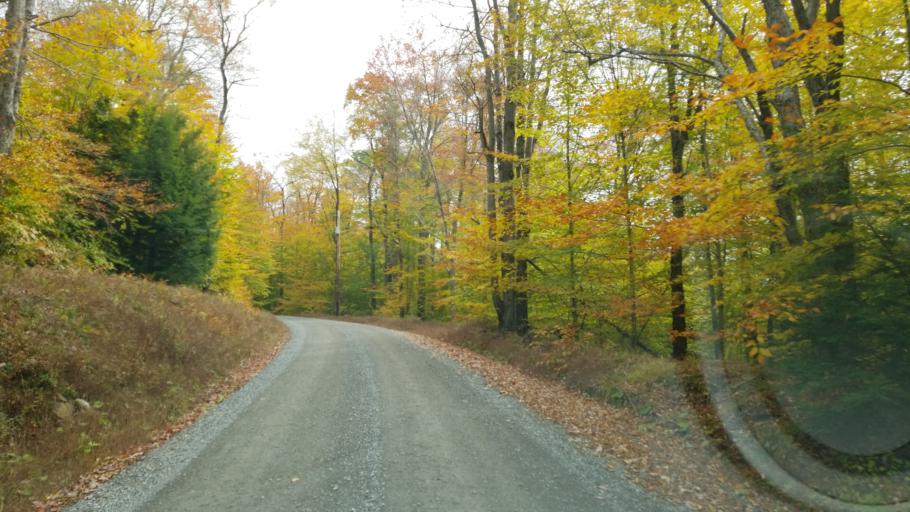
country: US
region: Pennsylvania
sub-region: Clearfield County
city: Clearfield
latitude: 41.1956
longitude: -78.4020
